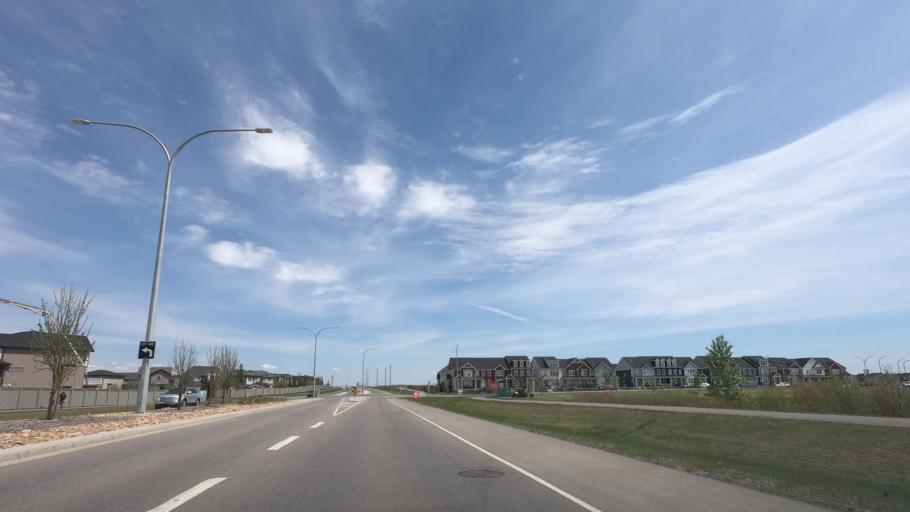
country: CA
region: Alberta
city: Airdrie
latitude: 51.2562
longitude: -114.0151
